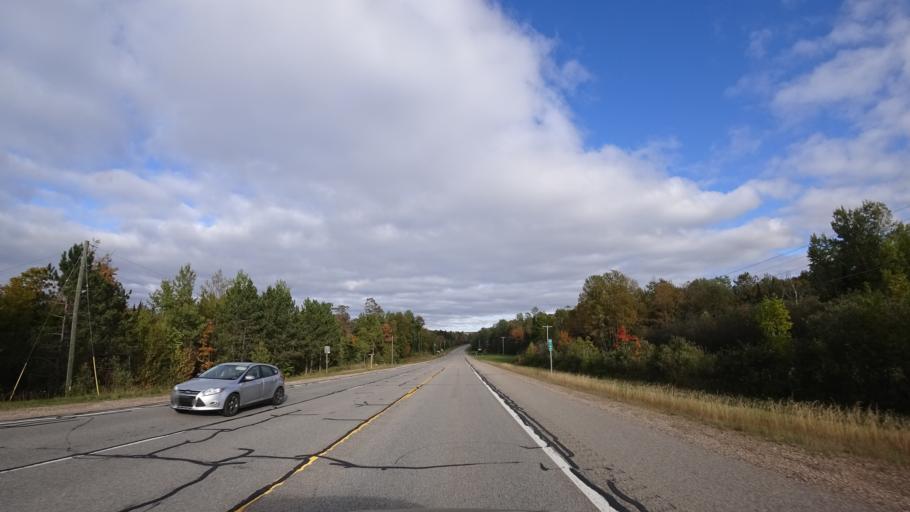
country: US
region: Michigan
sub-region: Alger County
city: Munising
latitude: 46.4414
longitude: -86.7474
